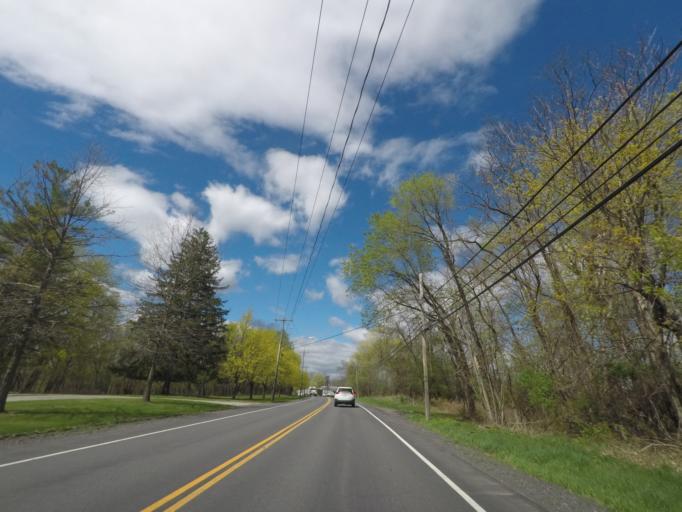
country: US
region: New York
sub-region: Columbia County
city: Oakdale
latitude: 42.2332
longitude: -73.7819
